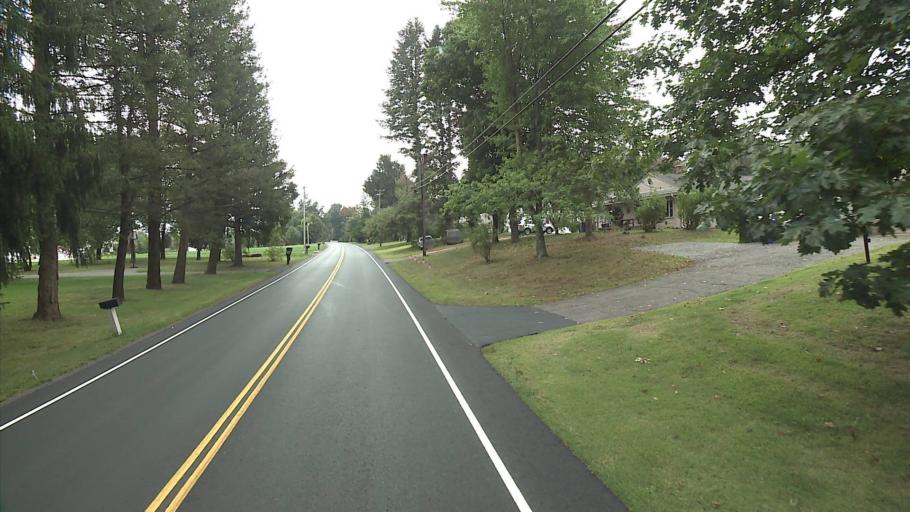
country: US
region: Connecticut
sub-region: Hartford County
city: Suffield Depot
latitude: 42.0221
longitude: -72.6913
